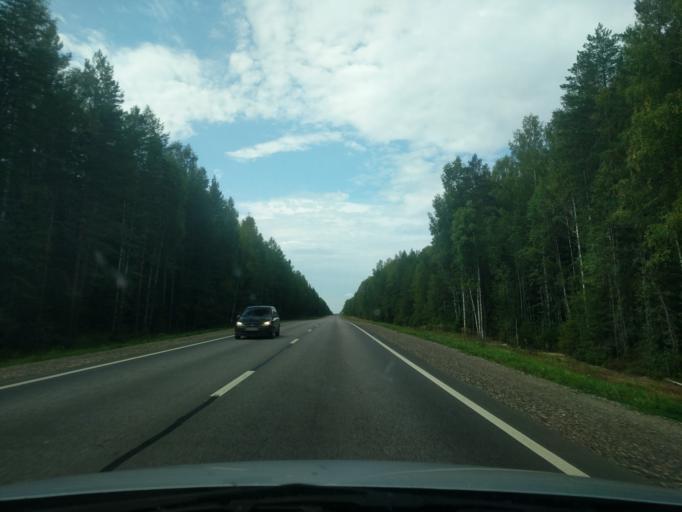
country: RU
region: Kostroma
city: Kadyy
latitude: 57.7958
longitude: 42.9277
